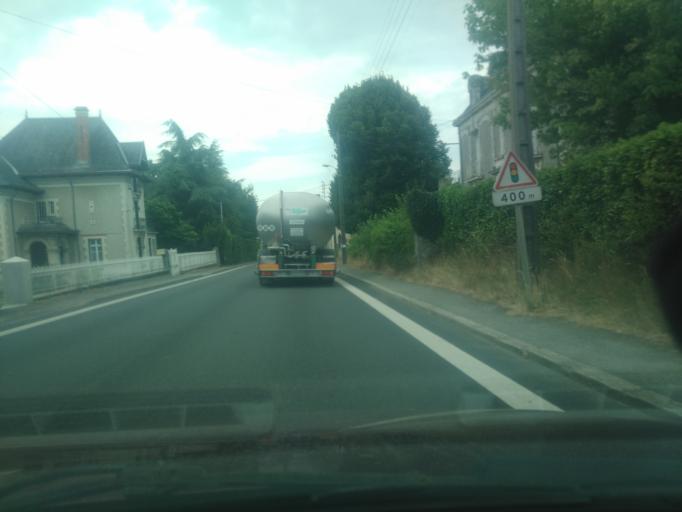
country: FR
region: Poitou-Charentes
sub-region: Departement des Deux-Sevres
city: Secondigny
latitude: 46.6090
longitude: -0.4133
